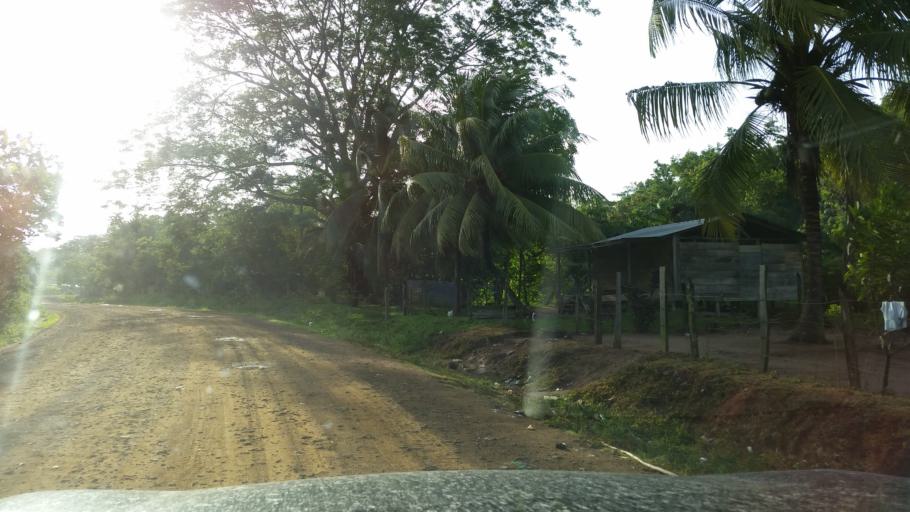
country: NI
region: Atlantico Norte (RAAN)
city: Puerto Cabezas
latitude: 14.0673
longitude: -83.9847
